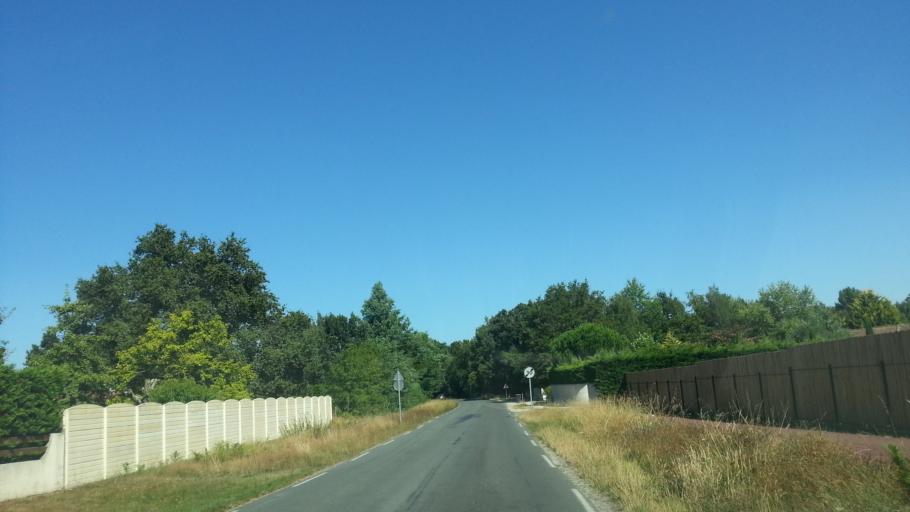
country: FR
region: Aquitaine
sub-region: Departement de la Gironde
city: Saint-Selve
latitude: 44.6824
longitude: -0.5070
